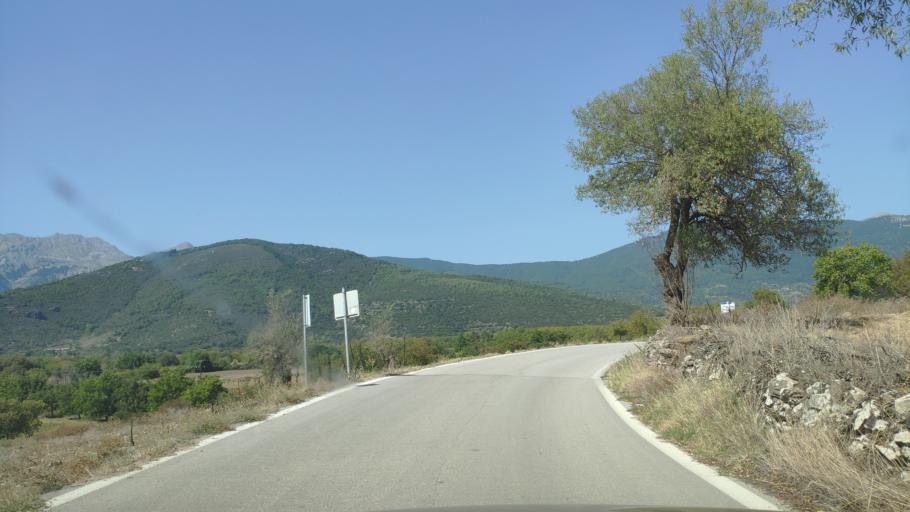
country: GR
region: West Greece
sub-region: Nomos Achaias
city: Aiyira
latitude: 37.9118
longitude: 22.3300
